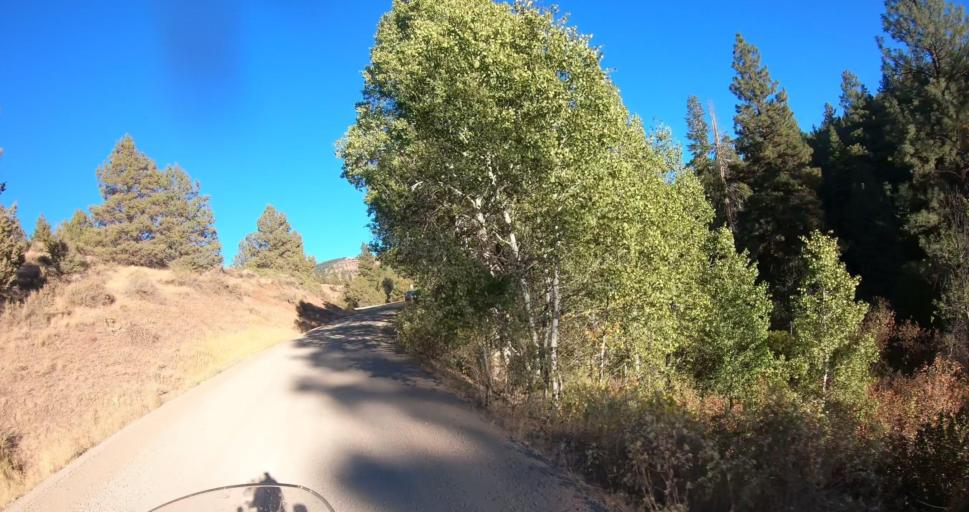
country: US
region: Oregon
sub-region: Lake County
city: Lakeview
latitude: 42.1926
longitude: -120.3229
